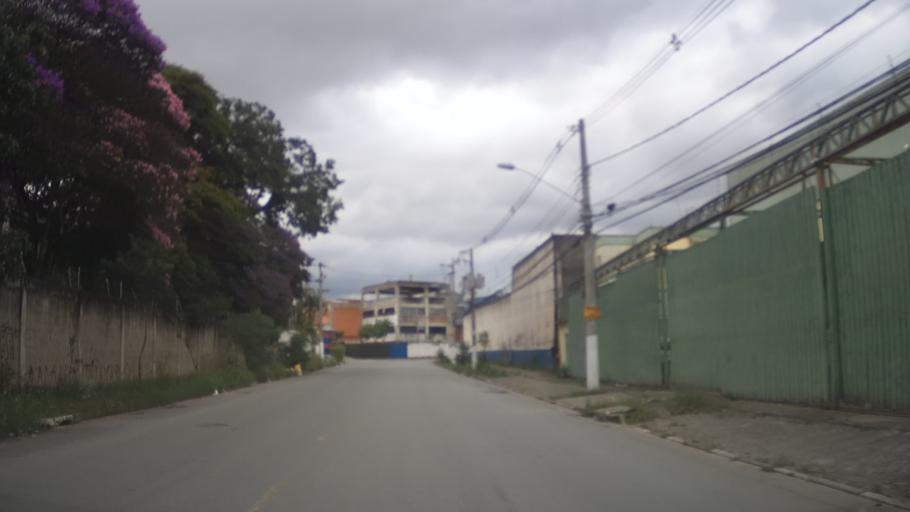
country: BR
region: Sao Paulo
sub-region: Guarulhos
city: Guarulhos
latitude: -23.4597
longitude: -46.4770
